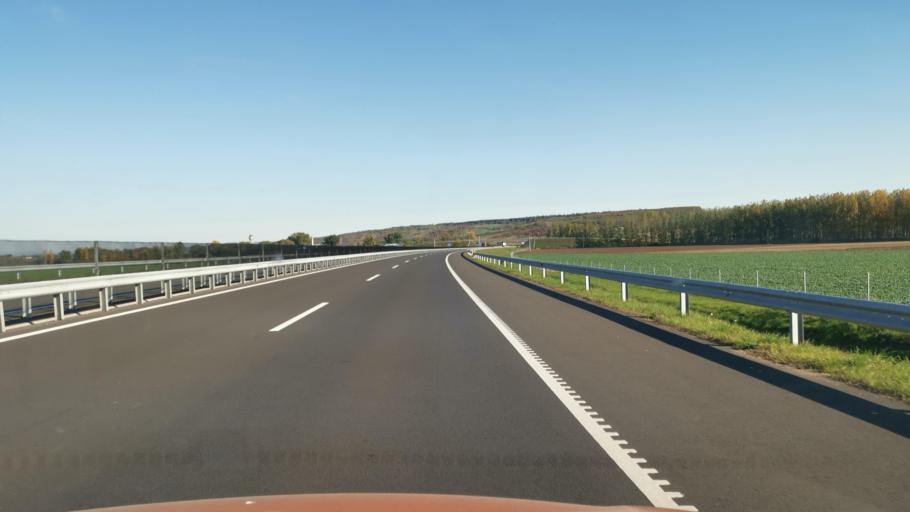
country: HU
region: Borsod-Abauj-Zemplen
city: Szikszo
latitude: 48.2029
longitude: 20.9095
